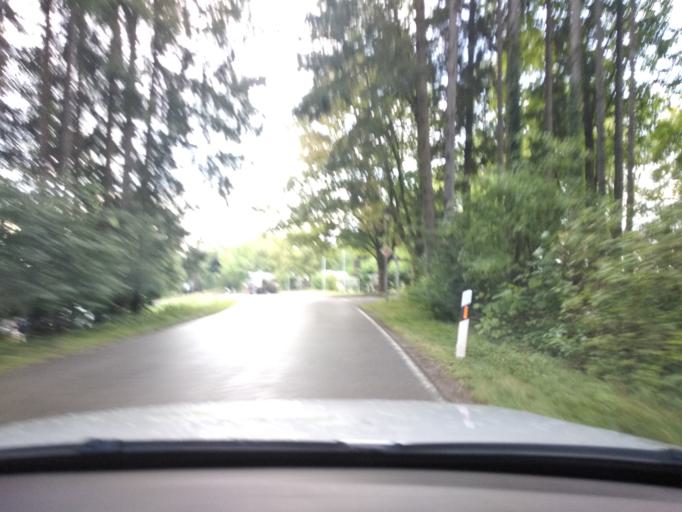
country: DE
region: Bavaria
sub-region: Swabia
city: Wolfertschwenden
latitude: 47.8687
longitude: 10.2230
